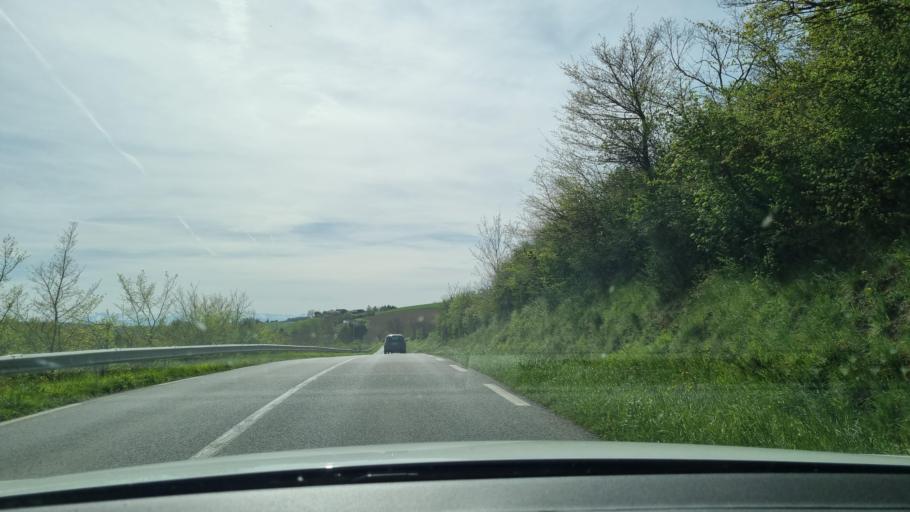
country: FR
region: Midi-Pyrenees
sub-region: Departement du Gers
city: Lombez
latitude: 43.4473
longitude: 0.8624
